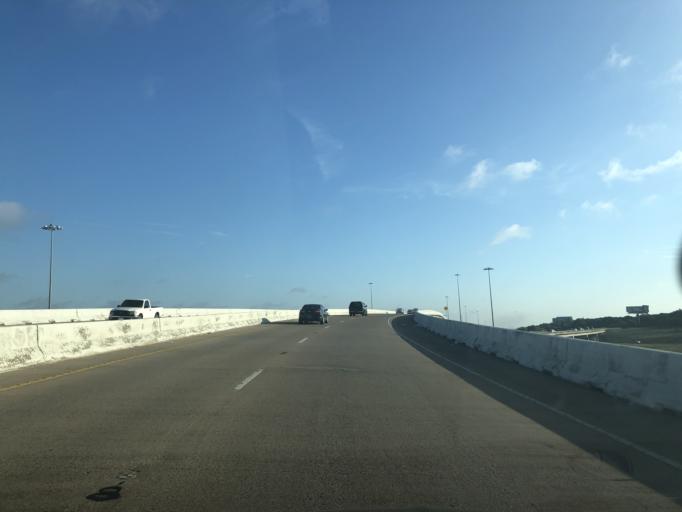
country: US
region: Texas
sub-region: Dallas County
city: Duncanville
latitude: 32.6695
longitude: -96.9472
